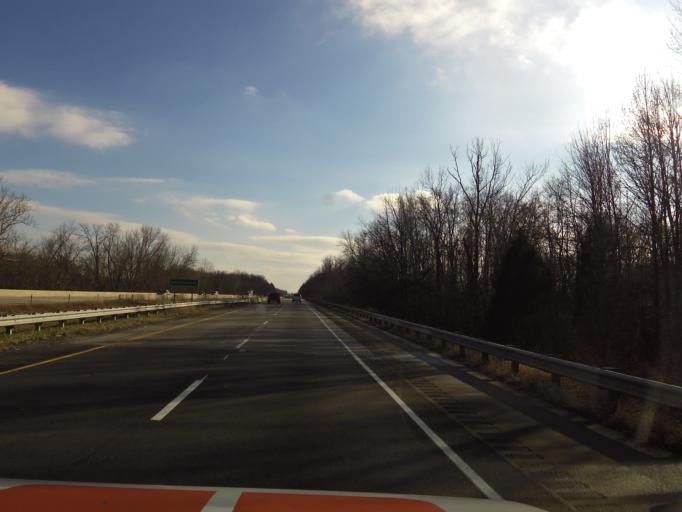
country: US
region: Indiana
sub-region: Scott County
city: Austin
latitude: 38.7648
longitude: -85.8308
